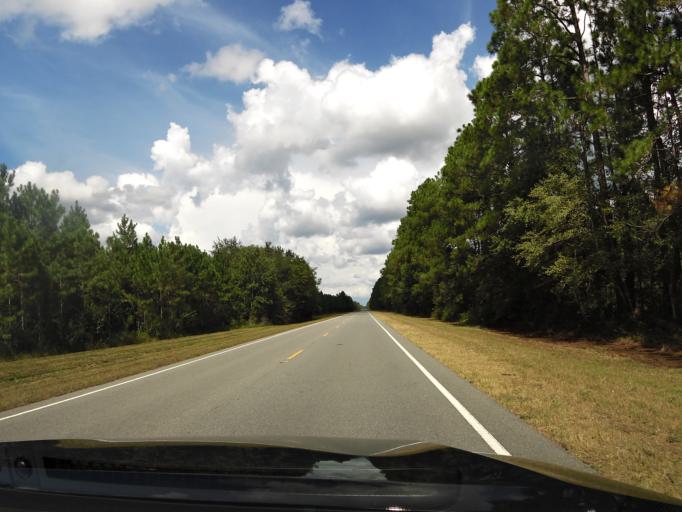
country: US
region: Georgia
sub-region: Charlton County
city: Folkston
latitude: 30.9713
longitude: -82.0246
